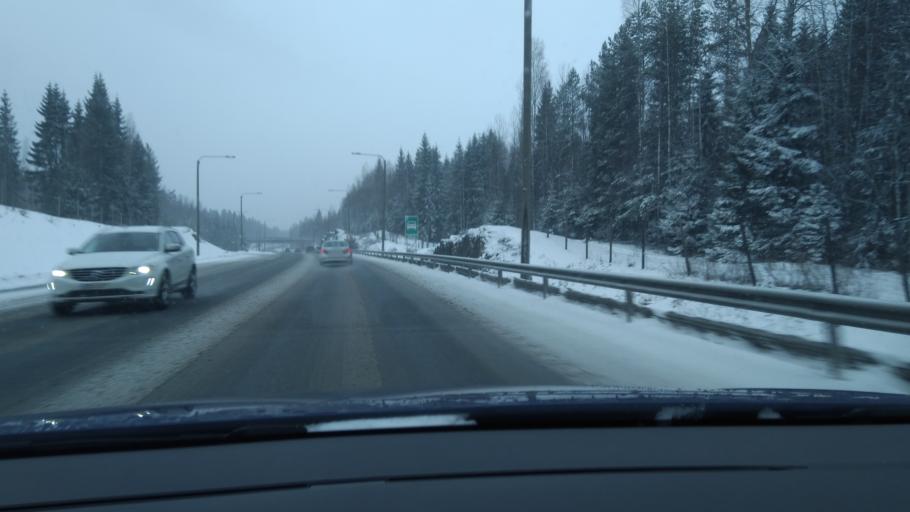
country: FI
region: Pirkanmaa
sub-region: Tampere
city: Kangasala
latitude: 61.5347
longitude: 23.9564
